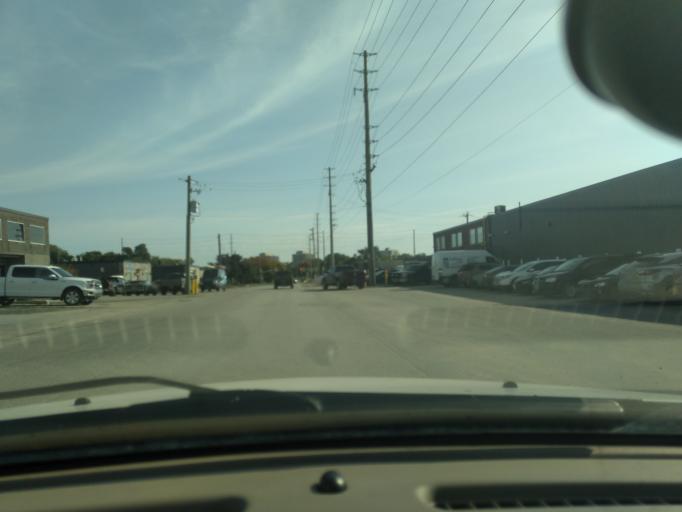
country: CA
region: Ontario
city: Barrie
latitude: 44.3766
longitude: -79.7034
